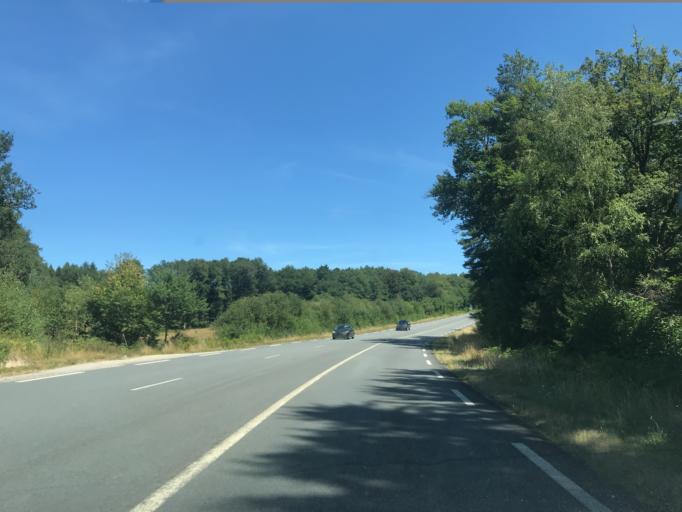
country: FR
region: Limousin
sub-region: Departement de la Correze
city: Egletons
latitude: 45.4298
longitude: 2.0820
